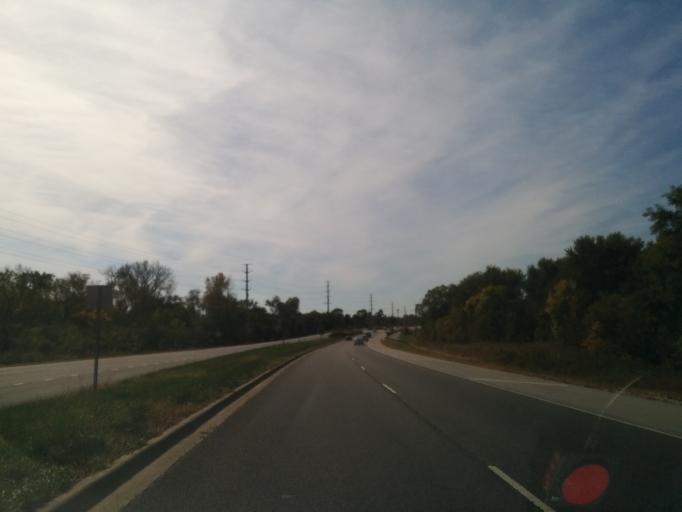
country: US
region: Illinois
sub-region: DuPage County
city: Warrenville
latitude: 41.8271
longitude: -88.1763
